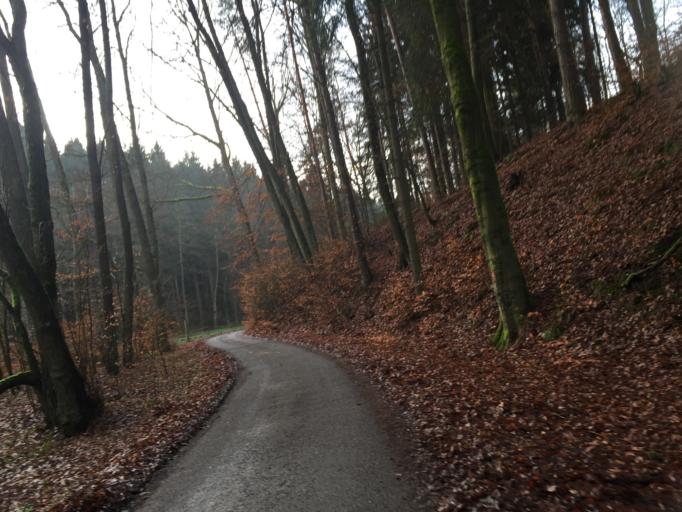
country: DE
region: Thuringia
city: Bollberg
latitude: 50.8868
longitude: 11.8082
